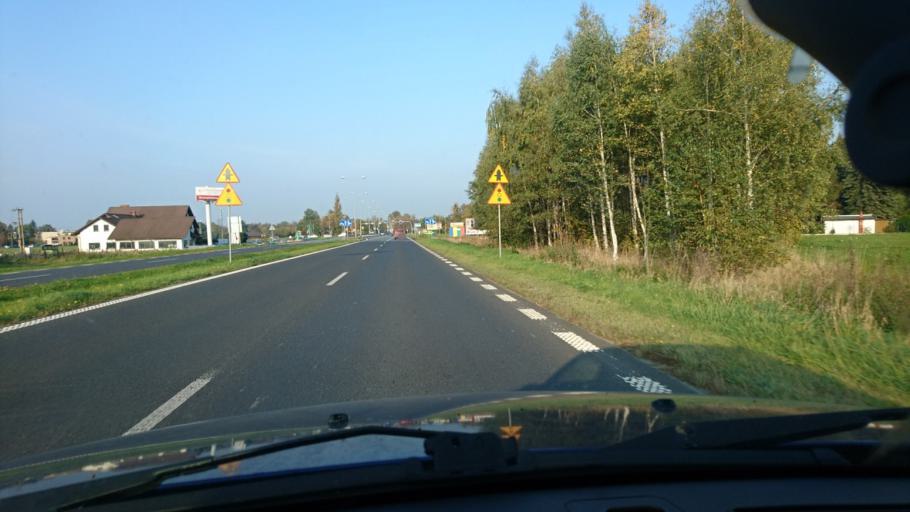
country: PL
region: Silesian Voivodeship
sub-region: Powiat cieszynski
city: Ustron
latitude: 49.7564
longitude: 18.8016
